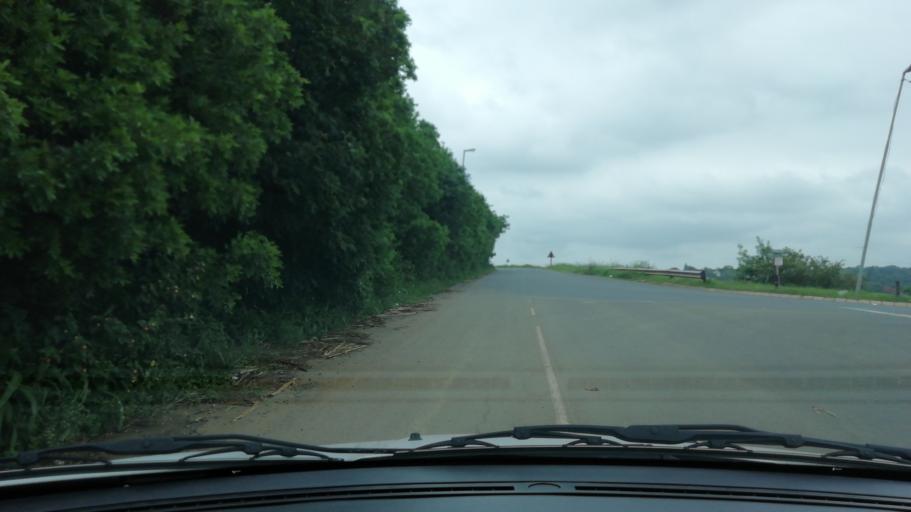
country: ZA
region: KwaZulu-Natal
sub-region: uThungulu District Municipality
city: Empangeni
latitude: -28.7381
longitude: 31.9071
